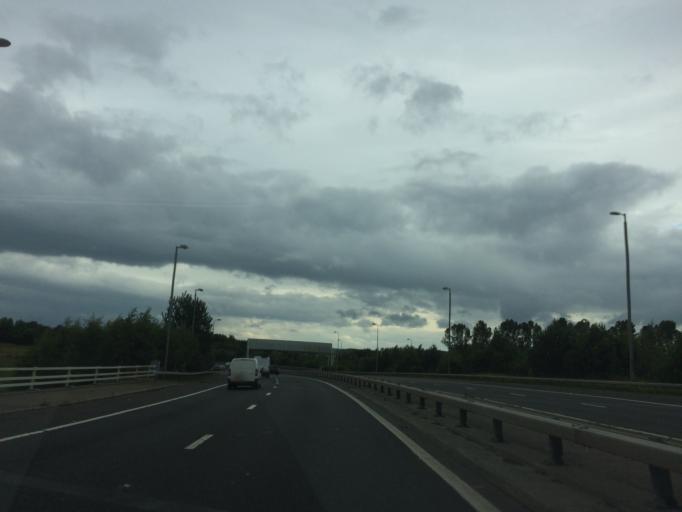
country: GB
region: Scotland
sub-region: East Renfrewshire
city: Giffnock
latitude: 55.8198
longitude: -4.3381
